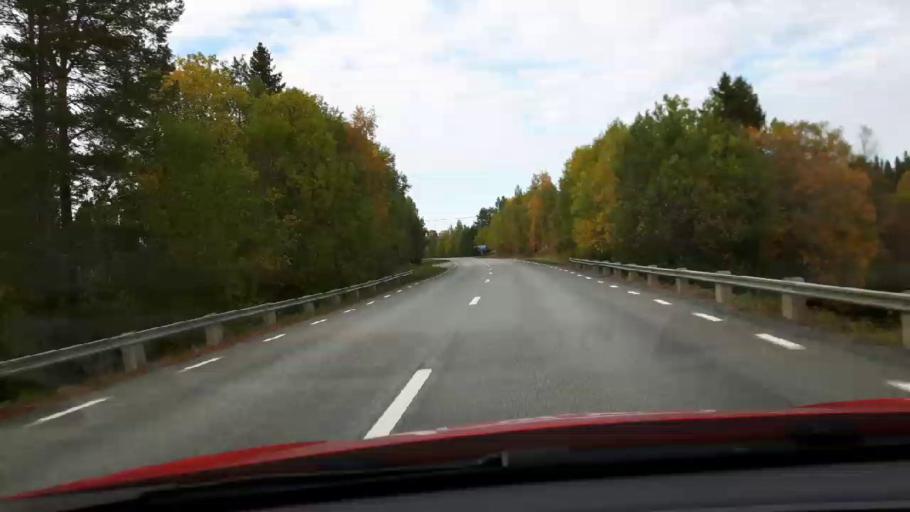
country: SE
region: Jaemtland
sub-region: Krokoms Kommun
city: Valla
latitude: 63.2532
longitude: 13.9966
